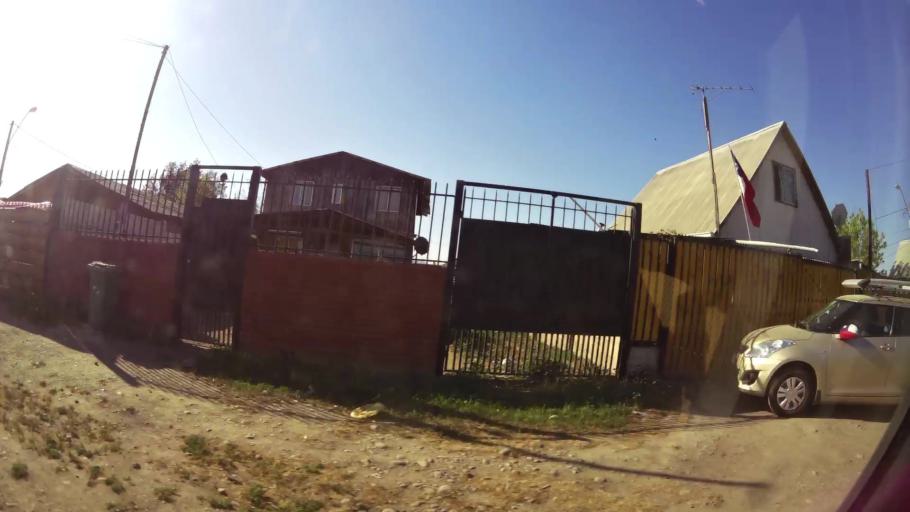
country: CL
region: Santiago Metropolitan
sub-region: Provincia de Talagante
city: Penaflor
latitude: -33.6161
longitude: -70.8730
